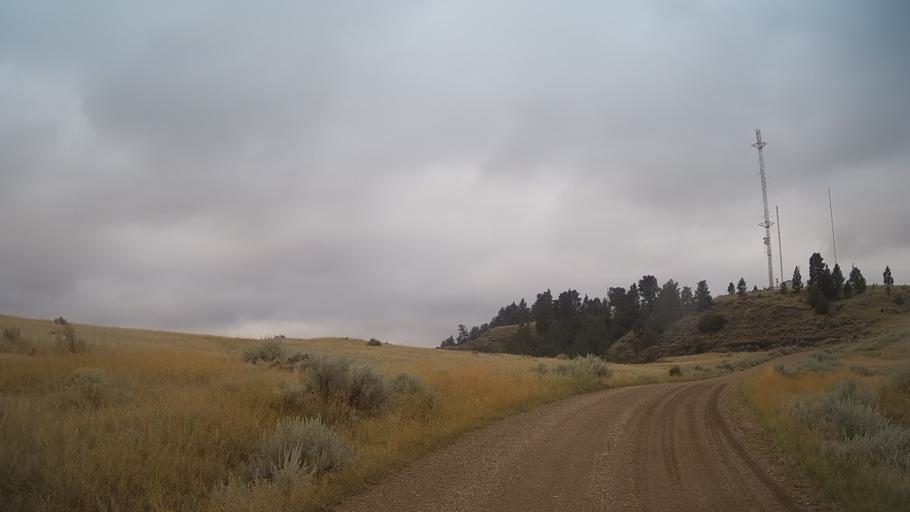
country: US
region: Montana
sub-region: Dawson County
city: Glendive
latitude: 47.0543
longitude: -104.6714
